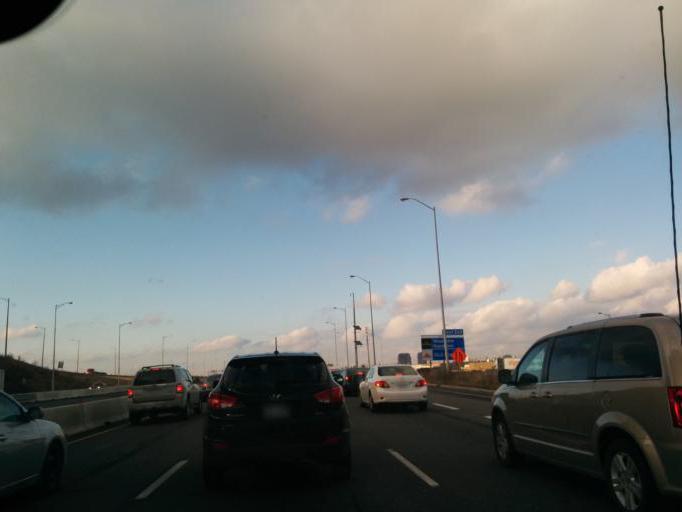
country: CA
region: Ontario
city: Etobicoke
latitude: 43.6978
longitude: -79.6074
